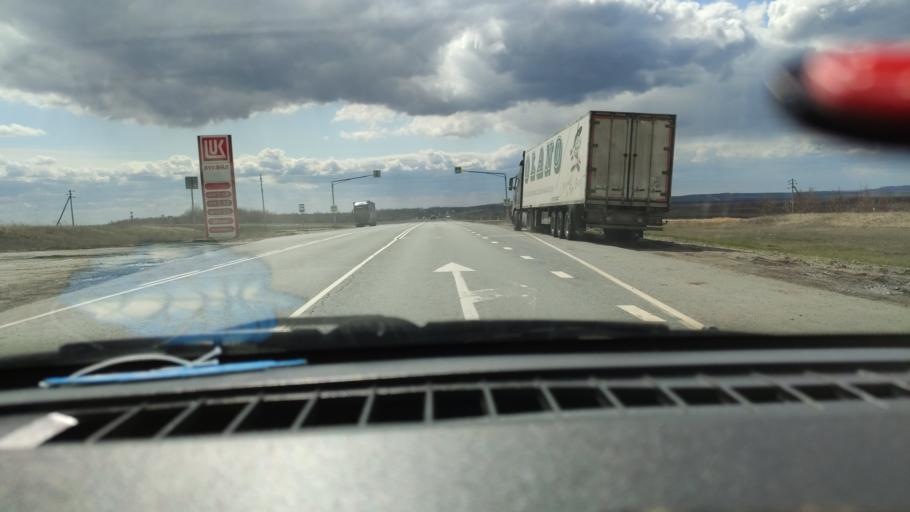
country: RU
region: Saratov
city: Alekseyevka
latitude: 52.2900
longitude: 47.9300
